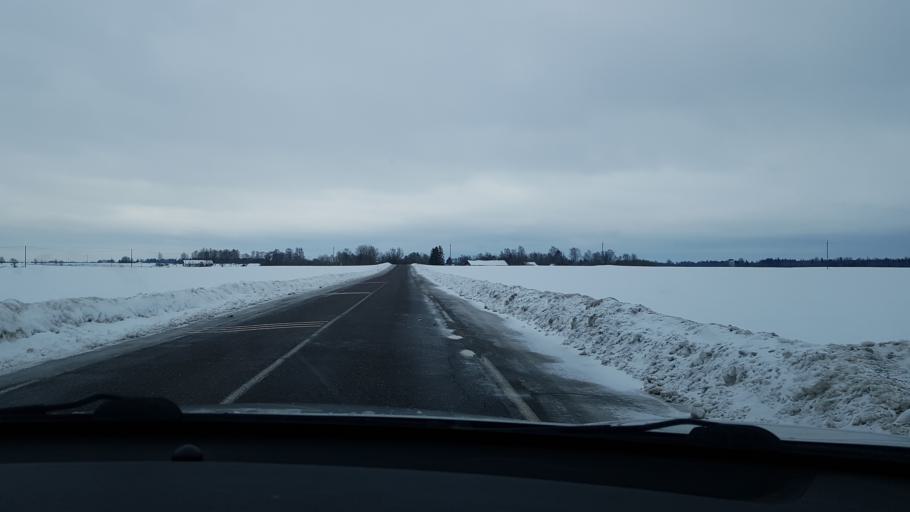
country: EE
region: Jaervamaa
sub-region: Koeru vald
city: Koeru
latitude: 58.9887
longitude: 25.9850
